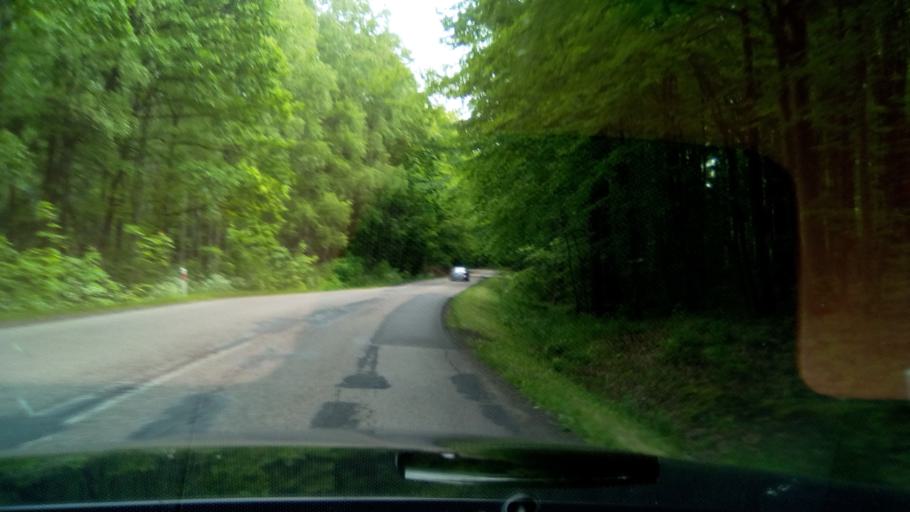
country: PL
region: Pomeranian Voivodeship
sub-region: Powiat bytowski
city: Bytow
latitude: 54.1001
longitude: 17.4618
